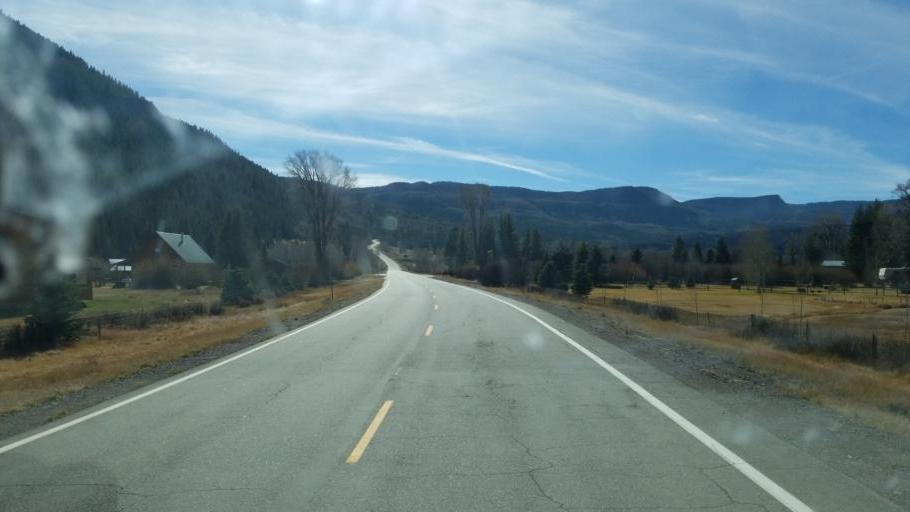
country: US
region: New Mexico
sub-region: Rio Arriba County
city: Chama
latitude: 37.1318
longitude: -106.3536
